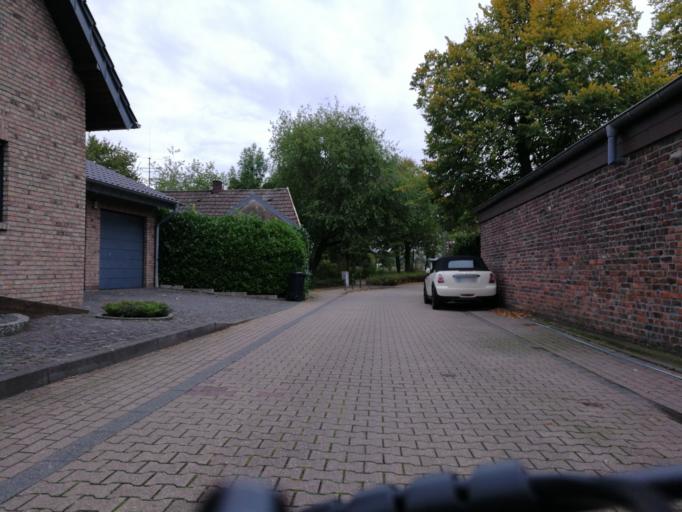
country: DE
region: North Rhine-Westphalia
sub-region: Regierungsbezirk Dusseldorf
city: Dusseldorf
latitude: 51.1478
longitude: 6.7526
